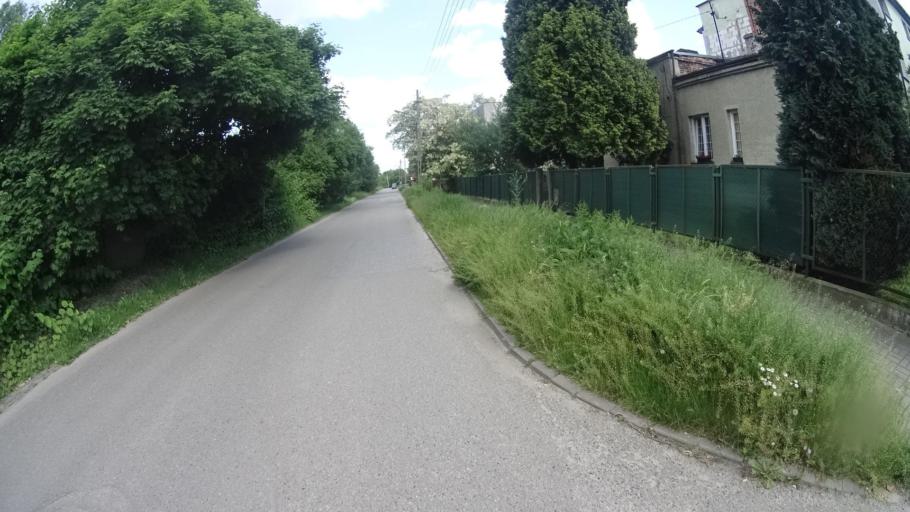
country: PL
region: Masovian Voivodeship
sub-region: Warszawa
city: Ursus
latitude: 52.2121
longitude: 20.9042
